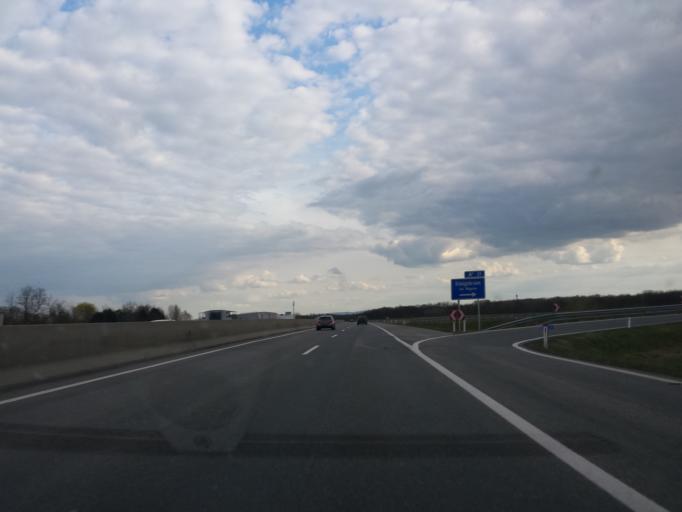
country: AT
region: Lower Austria
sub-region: Politischer Bezirk Tulln
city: Kirchberg am Wagram
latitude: 48.3923
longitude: 15.9172
